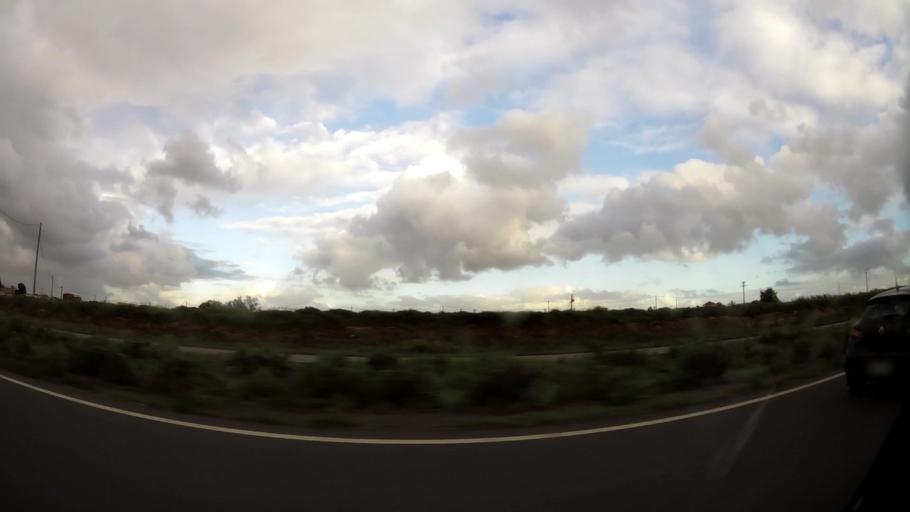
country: MA
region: Grand Casablanca
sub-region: Mohammedia
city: Mohammedia
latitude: 33.6218
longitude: -7.4311
